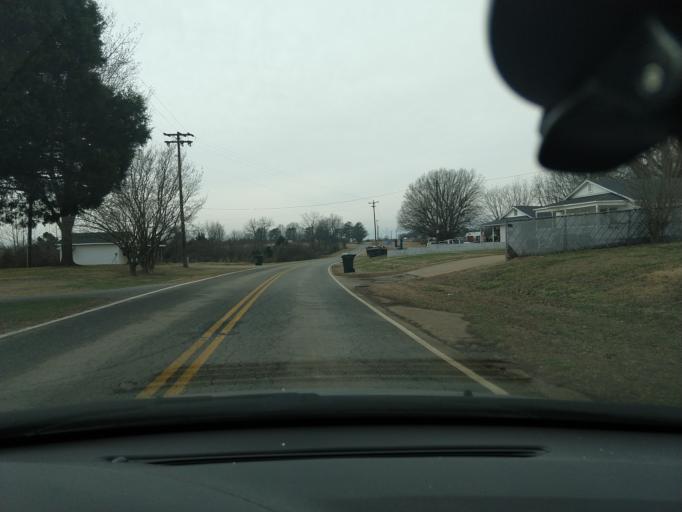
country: US
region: South Carolina
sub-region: Spartanburg County
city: Cowpens
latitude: 35.0659
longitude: -81.7672
